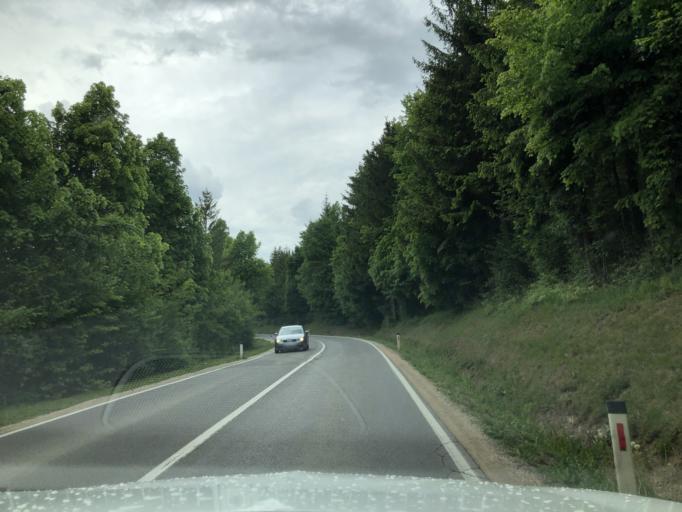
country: SI
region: Cerknica
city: Rakek
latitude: 45.7984
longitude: 14.3341
